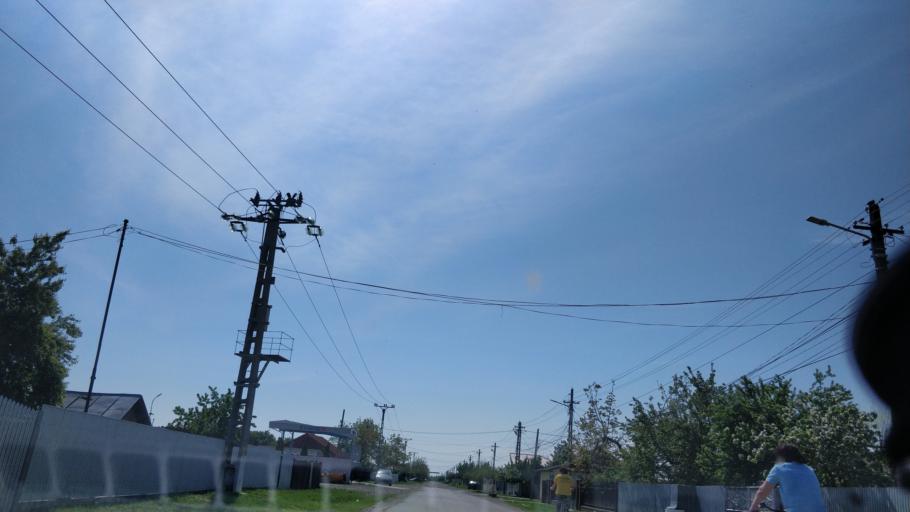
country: RO
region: Vrancea
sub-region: Comuna Suraia
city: Suraia
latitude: 45.6693
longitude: 27.3882
